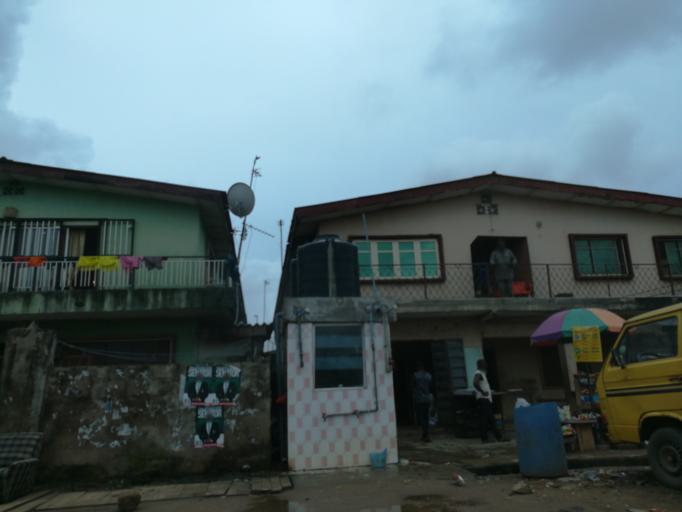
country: NG
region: Lagos
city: Agege
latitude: 6.6094
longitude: 3.3168
